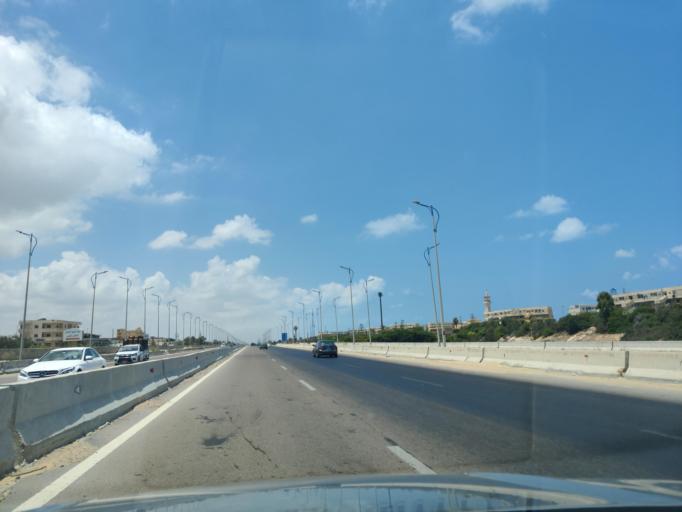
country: EG
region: Muhafazat Matruh
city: Al `Alamayn
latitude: 30.9343
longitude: 29.4859
